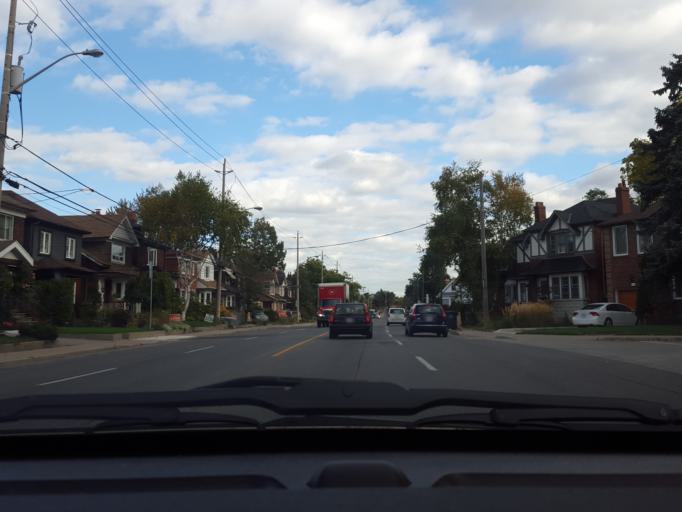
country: CA
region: Ontario
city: Toronto
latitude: 43.6970
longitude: -79.3485
